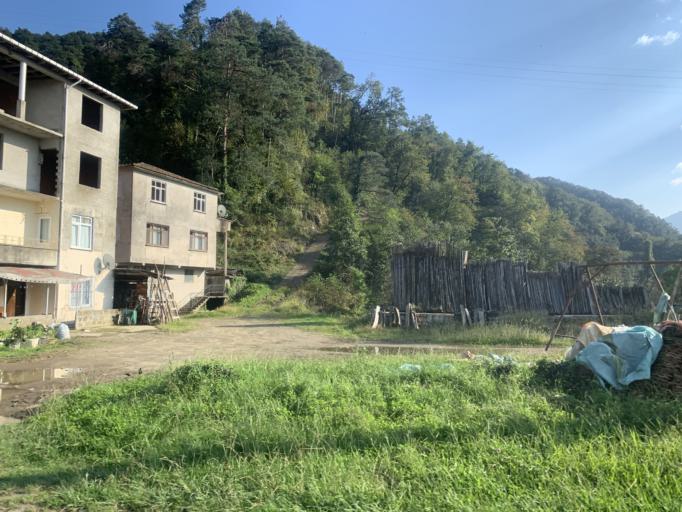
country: TR
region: Trabzon
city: Of
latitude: 40.9301
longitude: 40.2356
